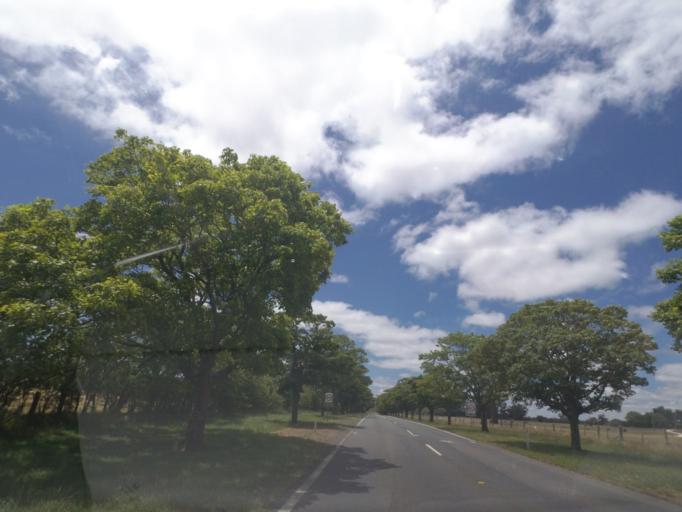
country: AU
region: Victoria
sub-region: Mount Alexander
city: Castlemaine
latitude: -37.3377
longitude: 144.1610
